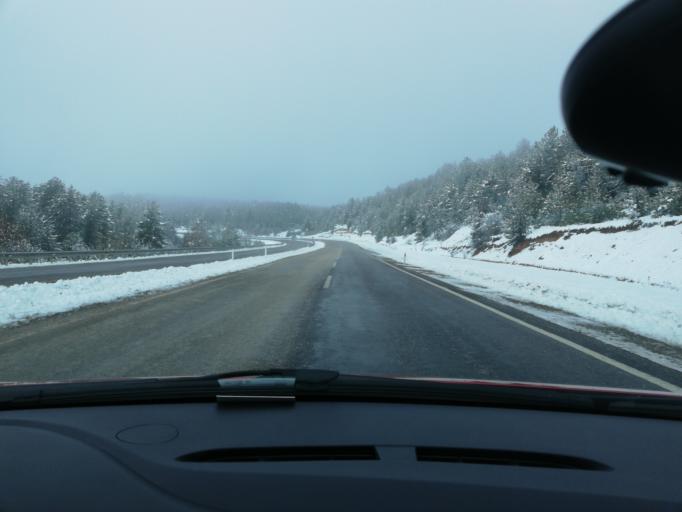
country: TR
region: Kastamonu
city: Akkaya
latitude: 41.2997
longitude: 33.5360
